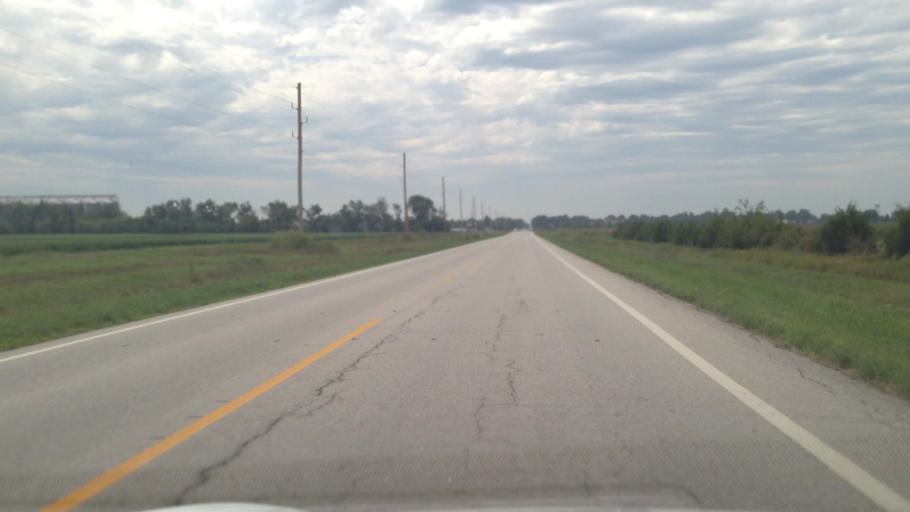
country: US
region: Kansas
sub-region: Allen County
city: Iola
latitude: 37.9321
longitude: -95.1701
